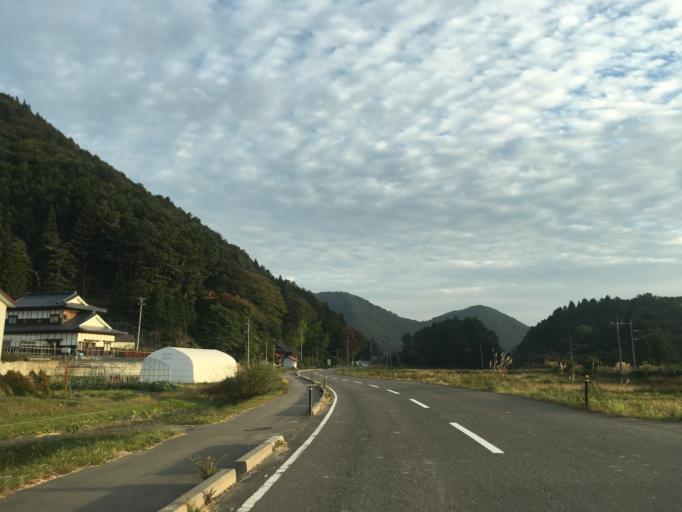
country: JP
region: Fukushima
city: Inawashiro
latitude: 37.5094
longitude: 140.1456
